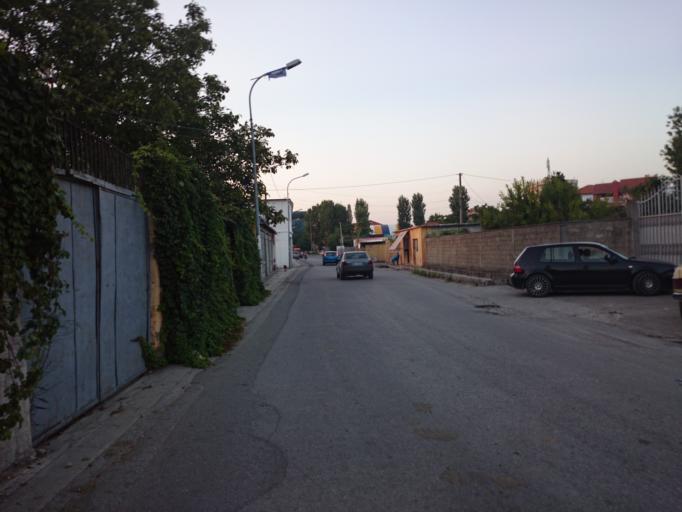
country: AL
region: Shkoder
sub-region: Rrethi i Shkodres
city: Shkoder
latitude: 42.0603
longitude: 19.5217
